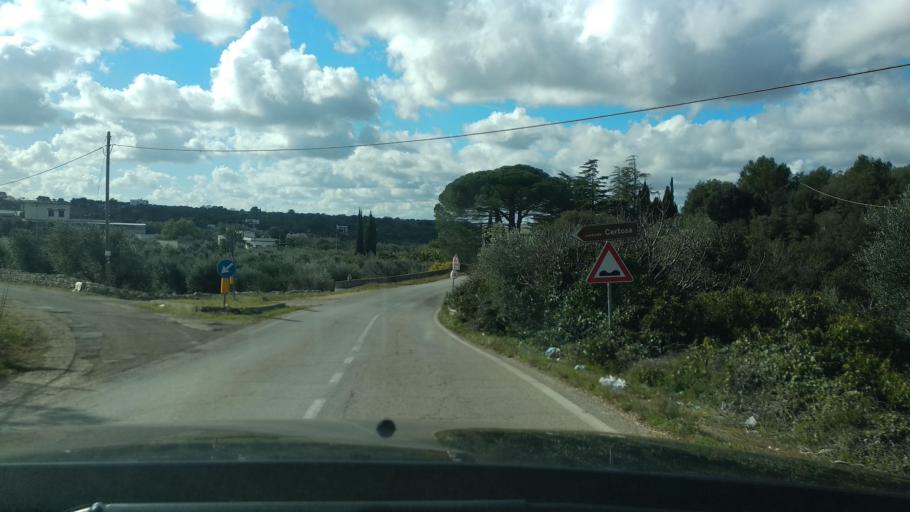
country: IT
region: Apulia
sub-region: Provincia di Brindisi
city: Ostuni
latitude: 40.7077
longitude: 17.5265
